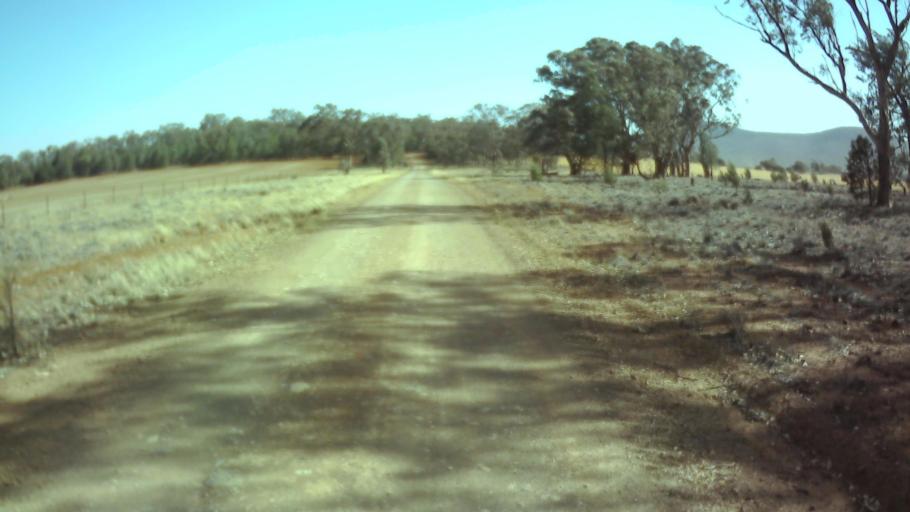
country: AU
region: New South Wales
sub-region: Weddin
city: Grenfell
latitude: -33.8581
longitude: 148.0155
